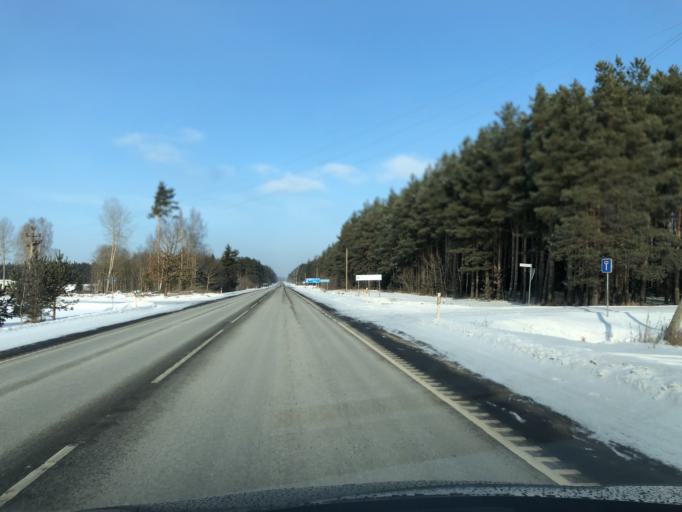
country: EE
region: Tartu
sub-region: Tartu linn
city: Tartu
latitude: 58.3839
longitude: 26.6717
